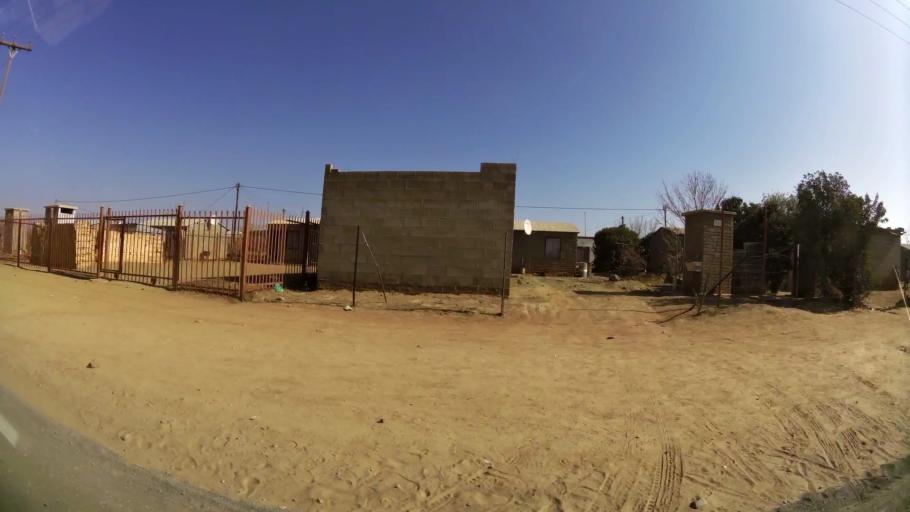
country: ZA
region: Orange Free State
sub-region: Mangaung Metropolitan Municipality
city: Bloemfontein
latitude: -29.1914
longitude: 26.2828
